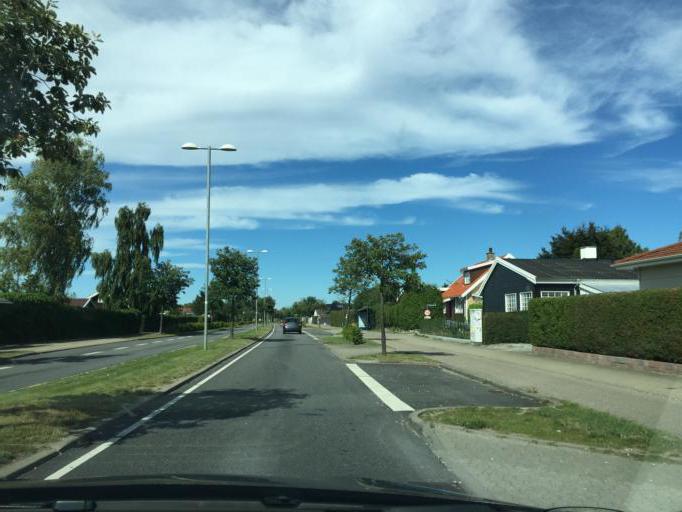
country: DK
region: Zealand
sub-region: Solrod Kommune
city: Solrod Strand
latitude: 55.5257
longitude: 12.2173
